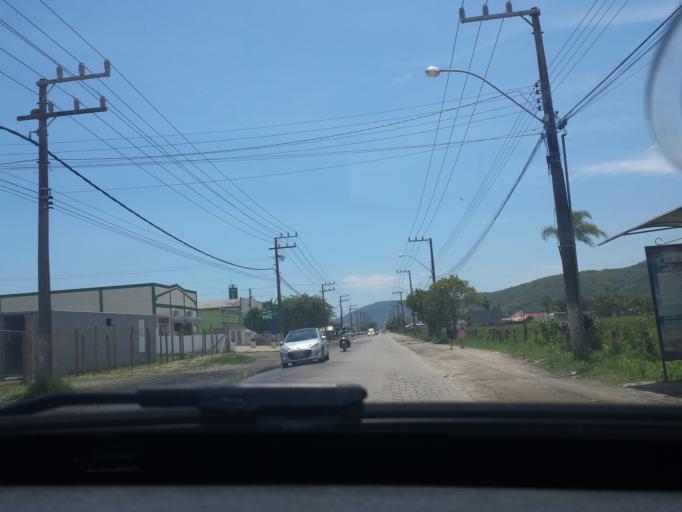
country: BR
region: Santa Catarina
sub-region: Porto Belo
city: Porto Belo
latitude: -27.1612
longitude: -48.5786
